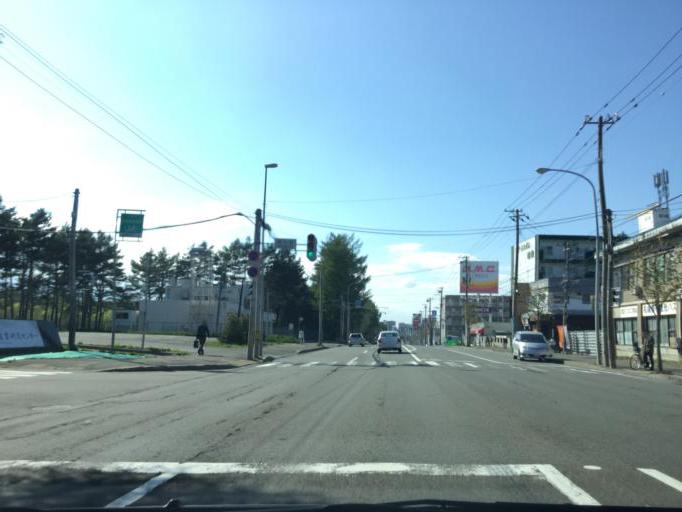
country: JP
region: Hokkaido
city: Sapporo
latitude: 43.0115
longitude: 141.4207
